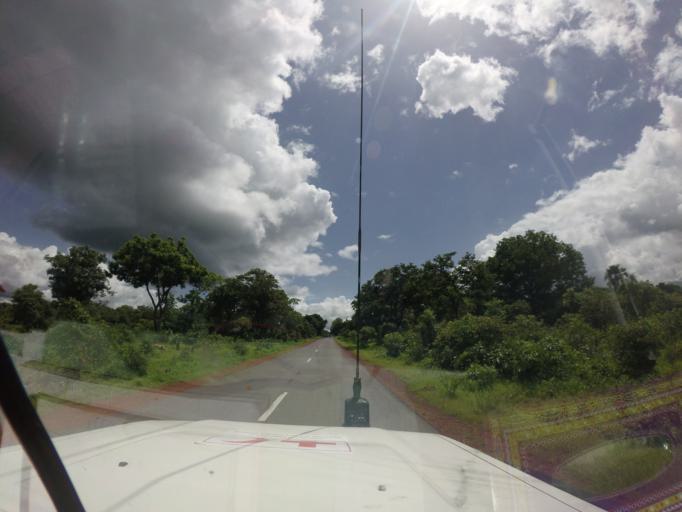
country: SL
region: Northern Province
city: Bindi
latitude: 10.1458
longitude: -11.5785
